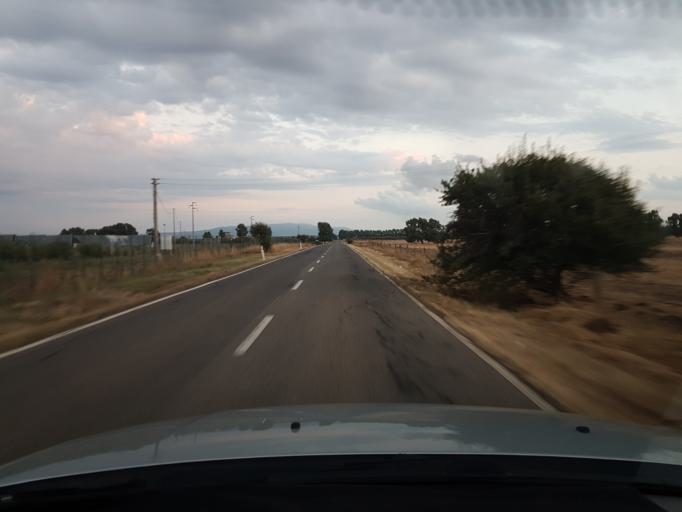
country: IT
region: Sardinia
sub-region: Provincia di Oristano
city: Milis
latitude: 40.0297
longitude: 8.6398
